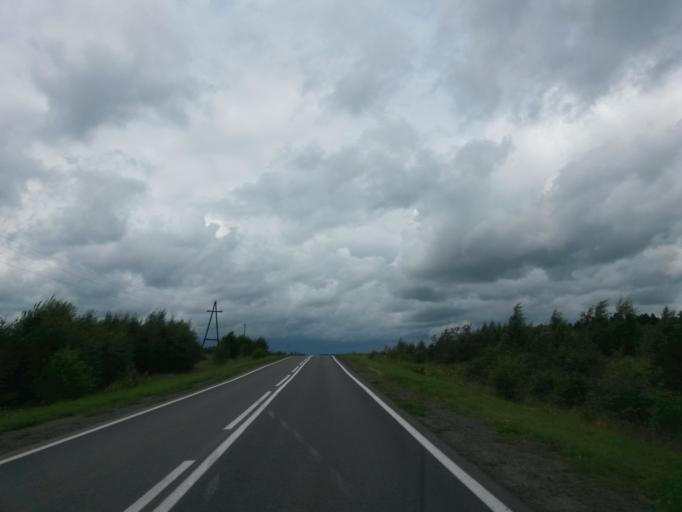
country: RU
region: Jaroslavl
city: Konstantinovskiy
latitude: 57.8179
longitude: 39.7077
